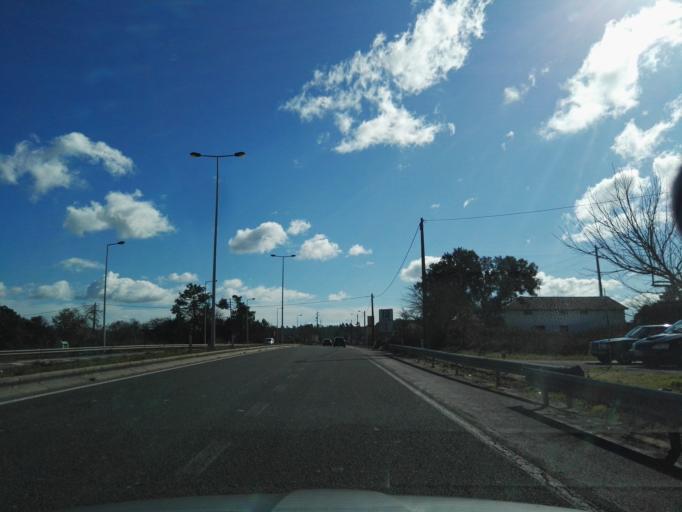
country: PT
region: Santarem
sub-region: Ourem
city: Fatima
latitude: 39.6292
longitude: -8.6819
